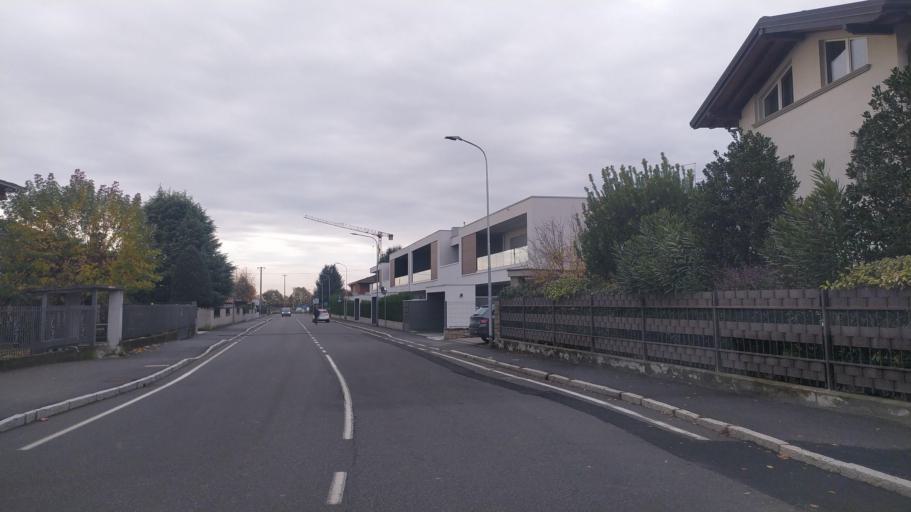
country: IT
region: Lombardy
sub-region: Provincia di Bergamo
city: Treviolo
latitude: 45.6675
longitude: 9.6094
